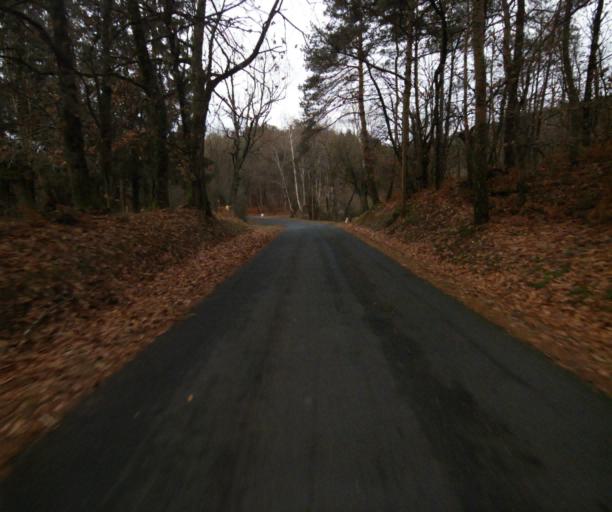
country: FR
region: Limousin
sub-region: Departement de la Correze
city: Cornil
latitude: 45.2323
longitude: 1.6562
